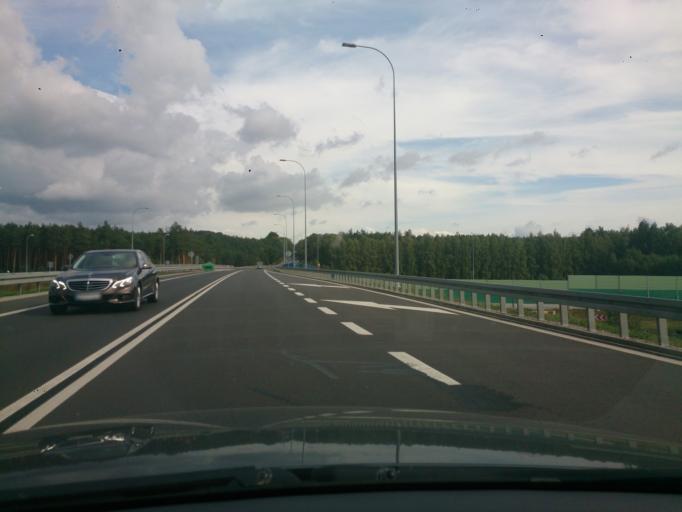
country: PL
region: Kujawsko-Pomorskie
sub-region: Powiat swiecki
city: Warlubie
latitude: 53.4644
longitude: 18.6182
